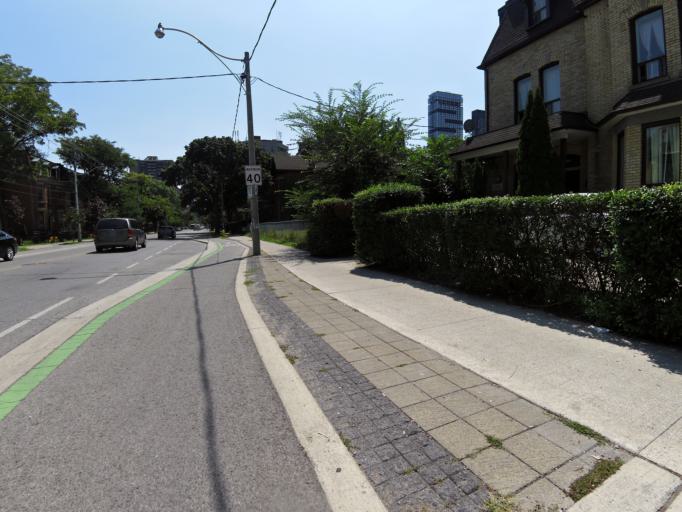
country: CA
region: Ontario
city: Toronto
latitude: 43.6607
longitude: -79.3721
